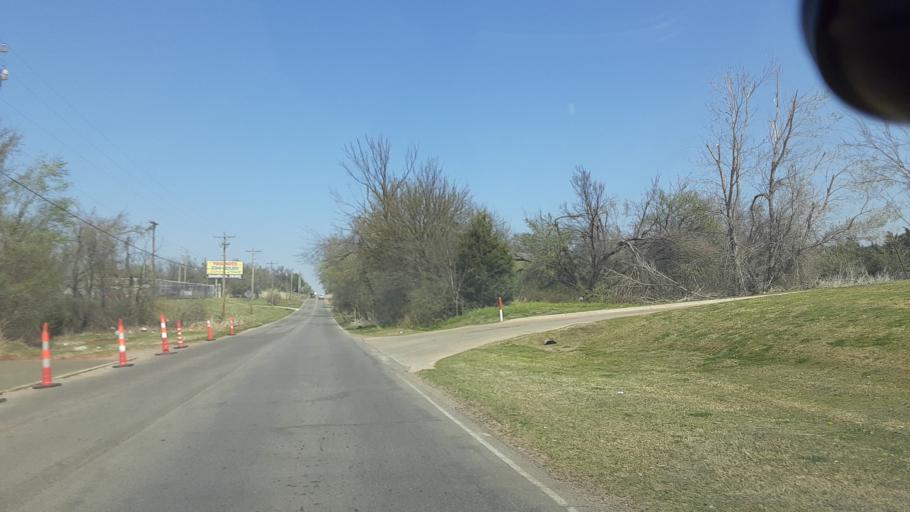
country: US
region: Oklahoma
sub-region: Oklahoma County
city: Edmond
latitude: 35.7260
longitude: -97.4784
